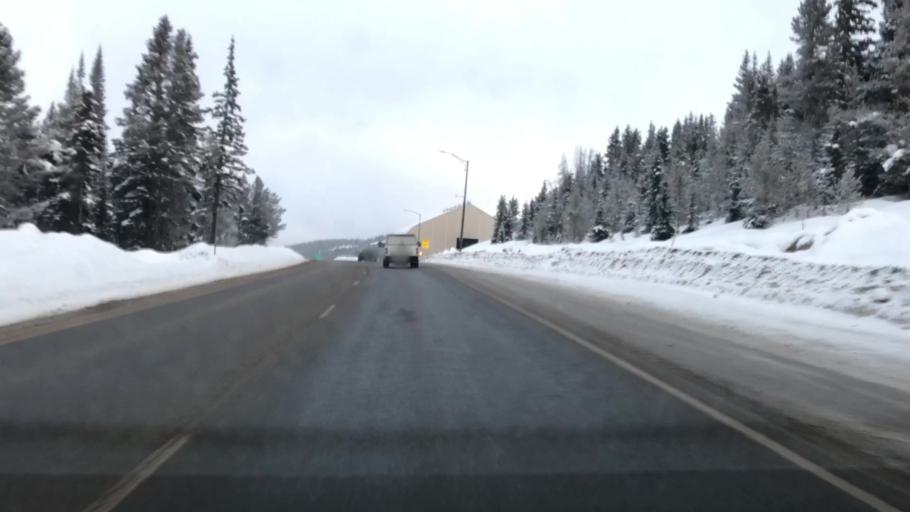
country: US
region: Colorado
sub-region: Summit County
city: Frisco
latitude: 39.5388
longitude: -106.2150
